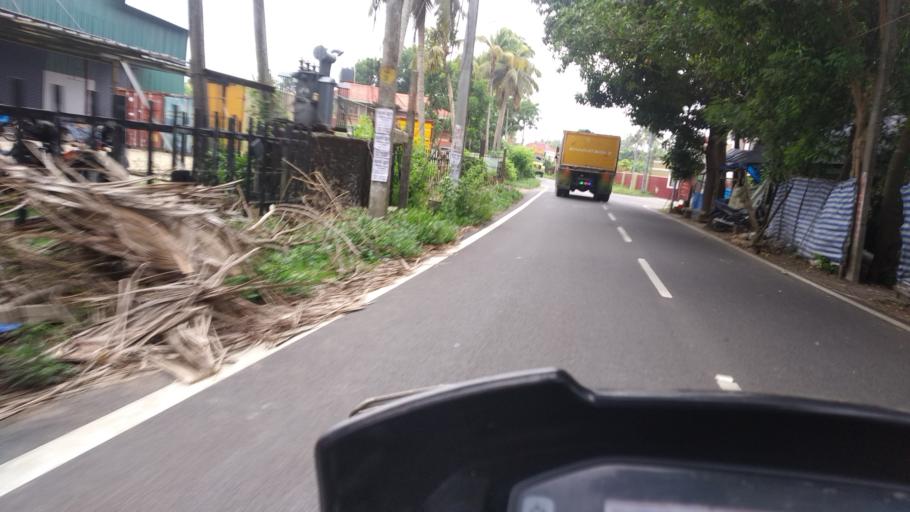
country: IN
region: Kerala
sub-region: Ernakulam
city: Aluva
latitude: 10.1550
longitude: 76.2877
